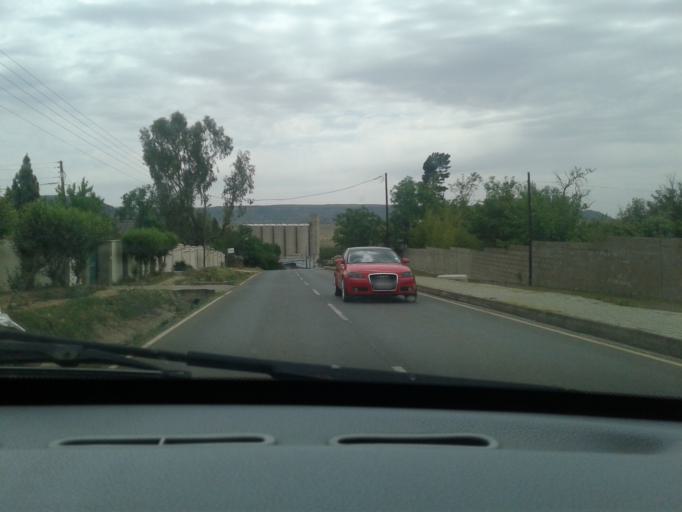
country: LS
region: Maseru
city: Maseru
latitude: -29.3016
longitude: 27.4797
